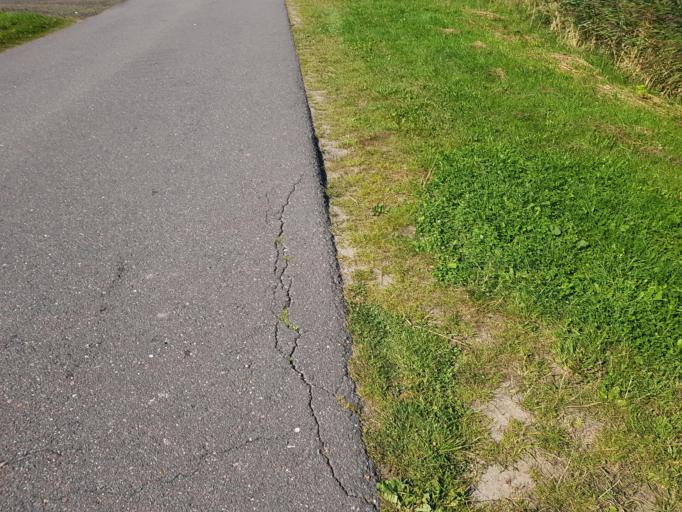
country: NL
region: North Holland
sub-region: Gemeente Texel
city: Den Burg
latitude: 53.1003
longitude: 4.8767
